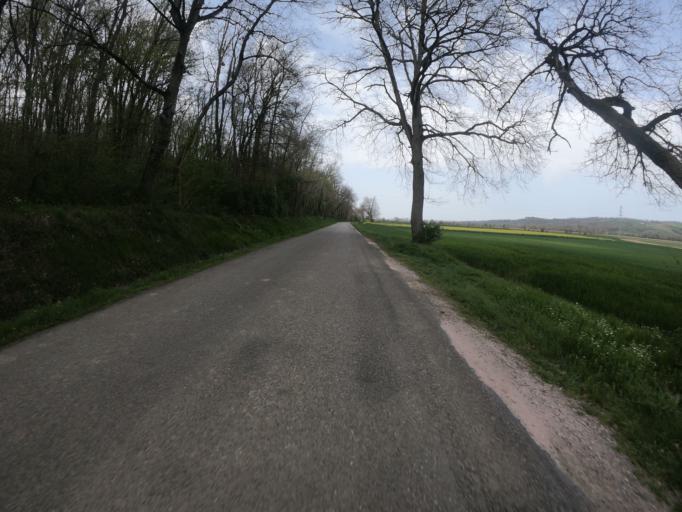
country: FR
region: Midi-Pyrenees
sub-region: Departement de l'Ariege
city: La Tour-du-Crieu
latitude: 43.1214
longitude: 1.7210
